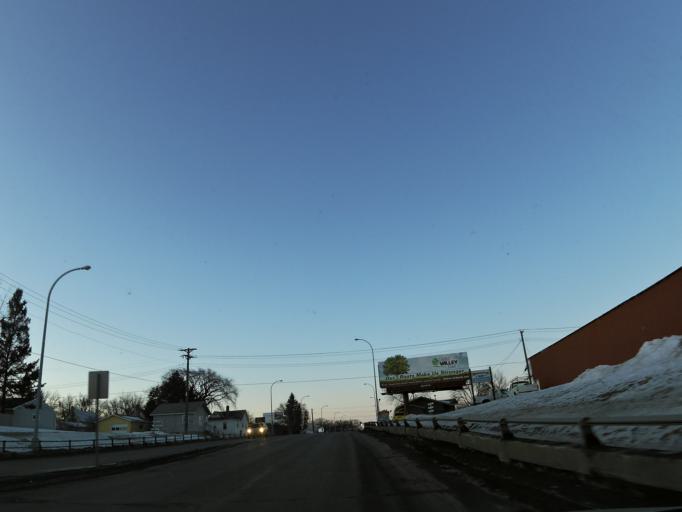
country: US
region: North Dakota
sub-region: Grand Forks County
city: Grand Forks
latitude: 47.9190
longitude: -97.0448
